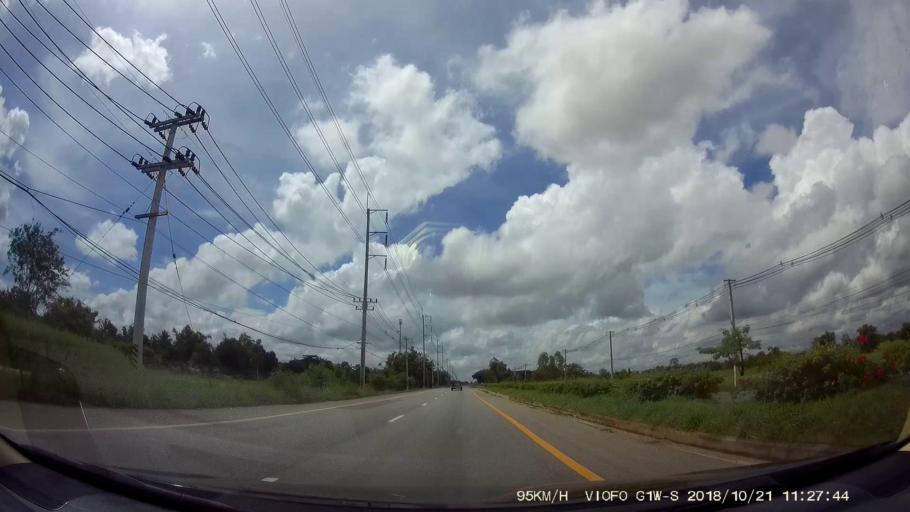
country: TH
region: Chaiyaphum
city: Chaiyaphum
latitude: 15.7973
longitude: 102.0531
